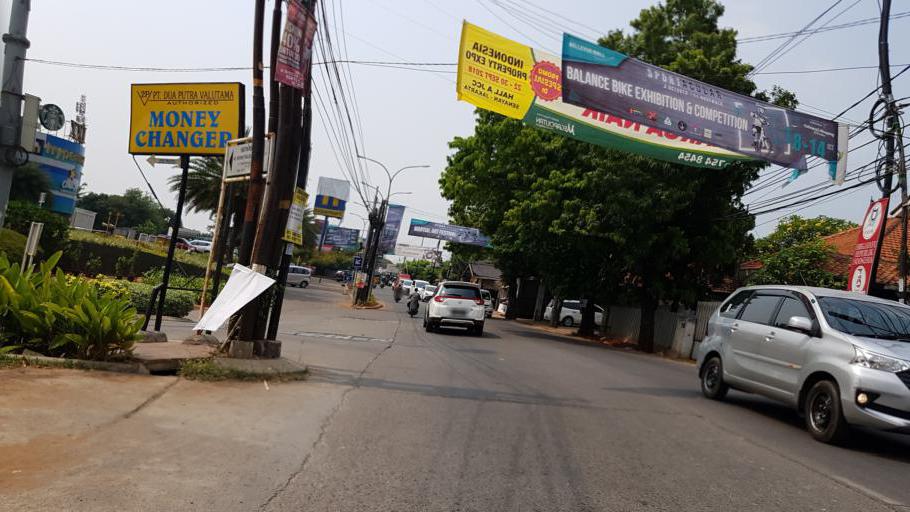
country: ID
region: West Java
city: Pamulang
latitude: -6.3177
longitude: 106.7833
